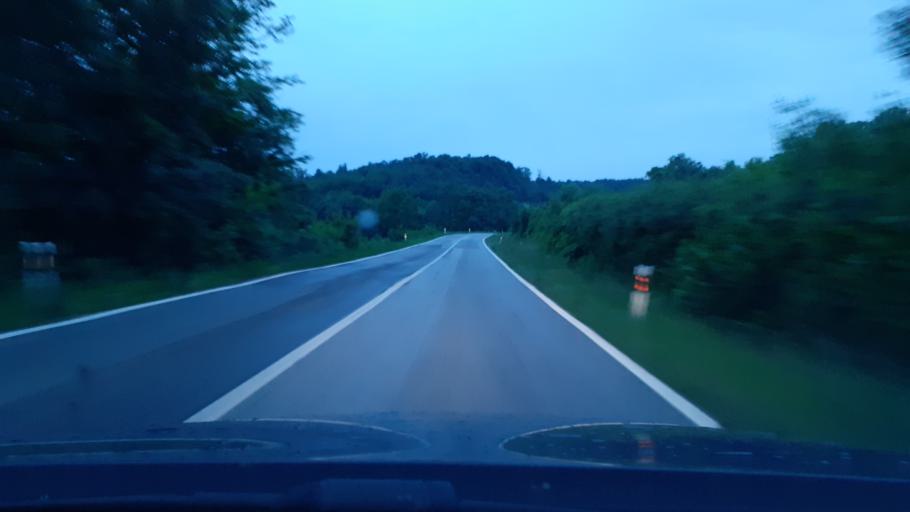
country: HR
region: Pozesko-Slavonska
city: Bilice
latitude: 45.1968
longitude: 17.8435
